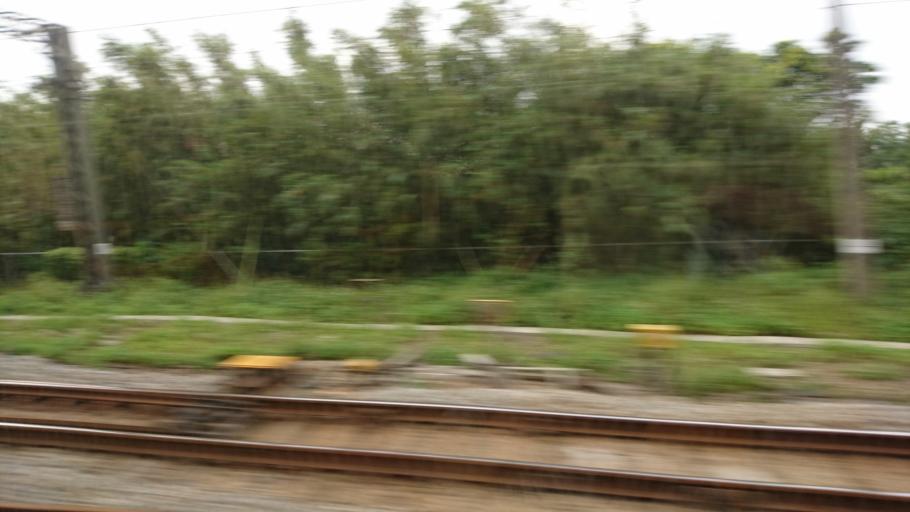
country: TW
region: Taiwan
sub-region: Hsinchu
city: Zhubei
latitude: 24.8425
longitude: 121.0117
